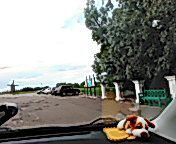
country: RU
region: Penza
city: Lermontovo
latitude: 52.9944
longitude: 43.6732
